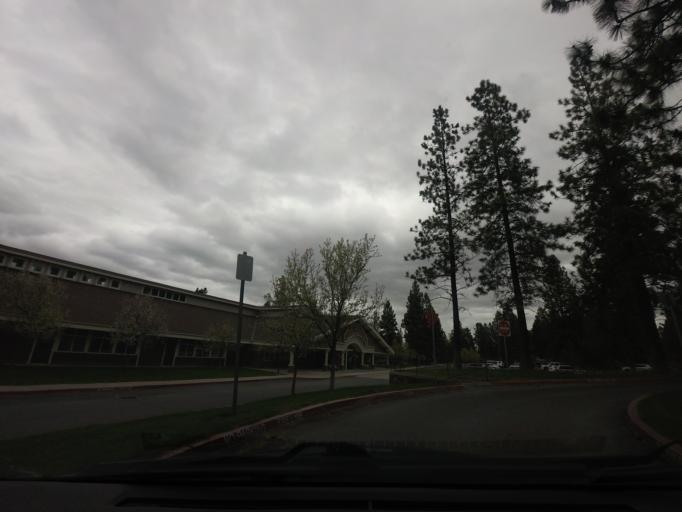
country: US
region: Oregon
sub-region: Deschutes County
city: Bend
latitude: 44.0229
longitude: -121.3311
